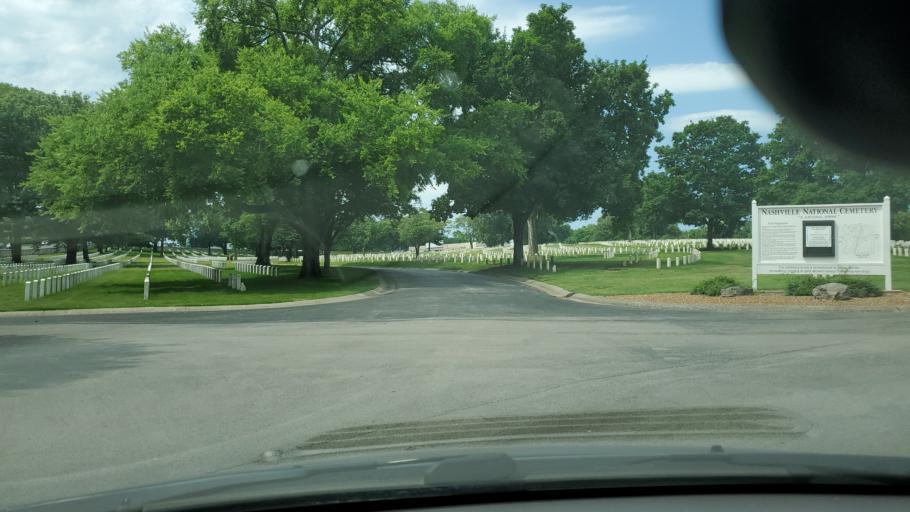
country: US
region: Tennessee
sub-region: Davidson County
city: Goodlettsville
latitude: 36.2418
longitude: -86.7237
